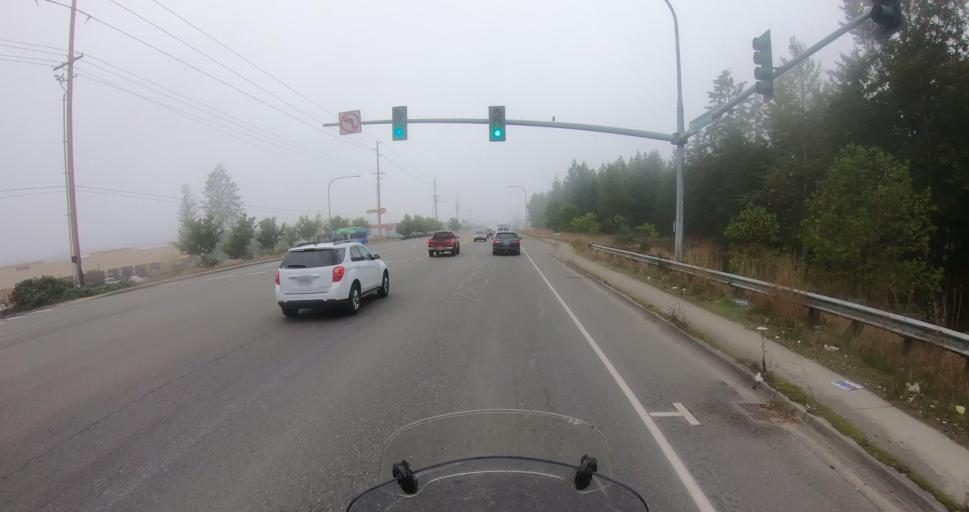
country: US
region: Washington
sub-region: Pierce County
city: Graham
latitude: 47.0999
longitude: -122.2938
